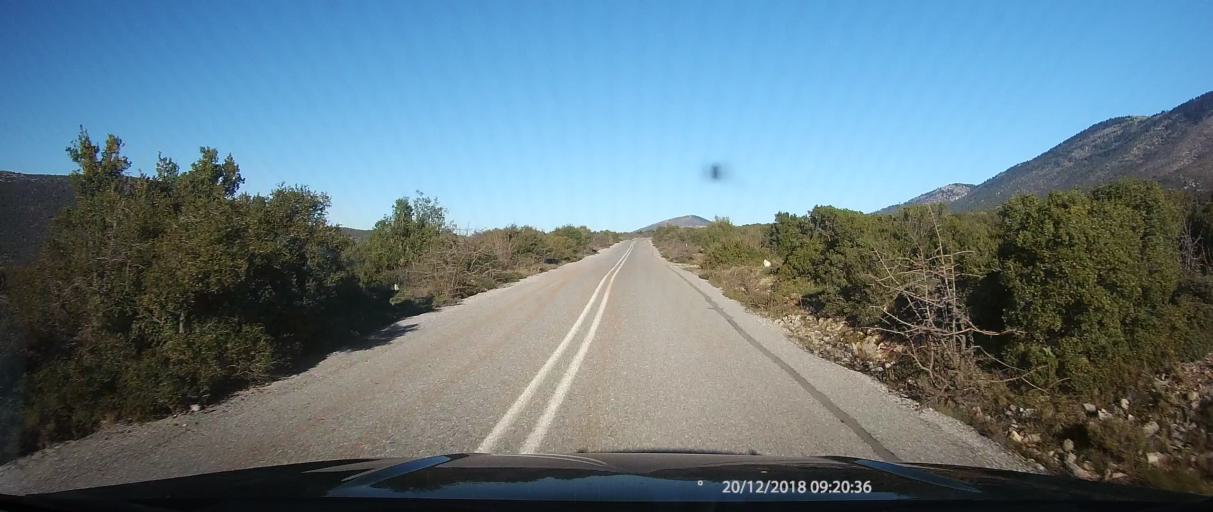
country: GR
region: Peloponnese
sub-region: Nomos Lakonias
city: Molaoi
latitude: 36.9317
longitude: 22.9222
